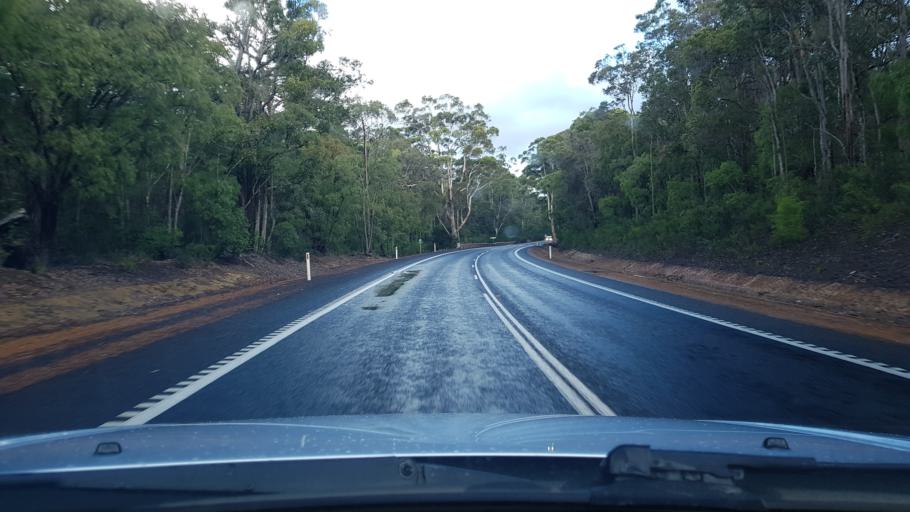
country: AU
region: Western Australia
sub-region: Augusta-Margaret River Shire
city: Margaret River
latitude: -33.9080
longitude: 115.0854
